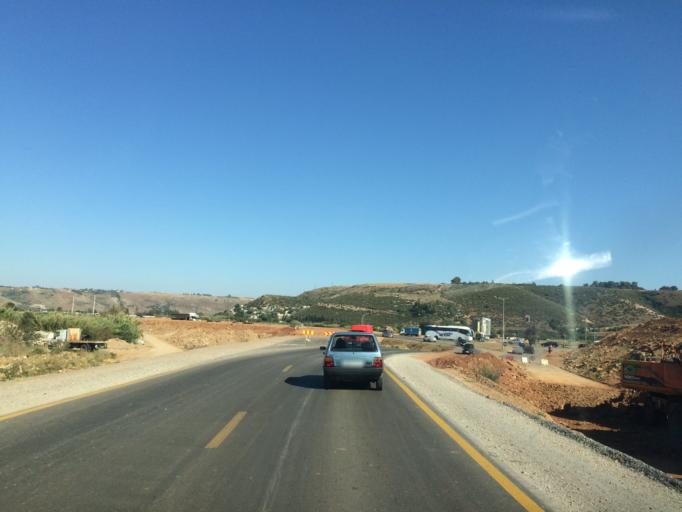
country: MA
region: Rabat-Sale-Zemmour-Zaer
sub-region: Rabat
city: Rabat
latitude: 33.9878
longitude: -6.7913
